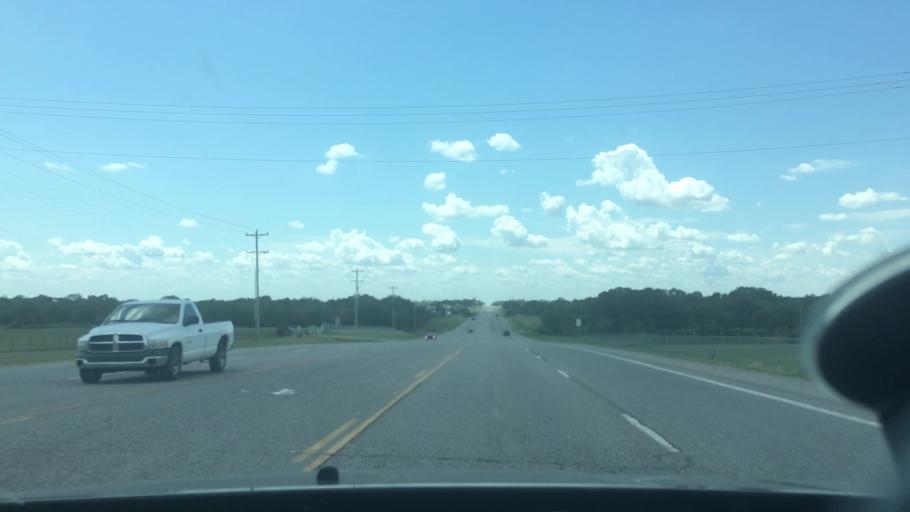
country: US
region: Oklahoma
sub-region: Bryan County
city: Calera
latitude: 33.9982
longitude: -96.4726
